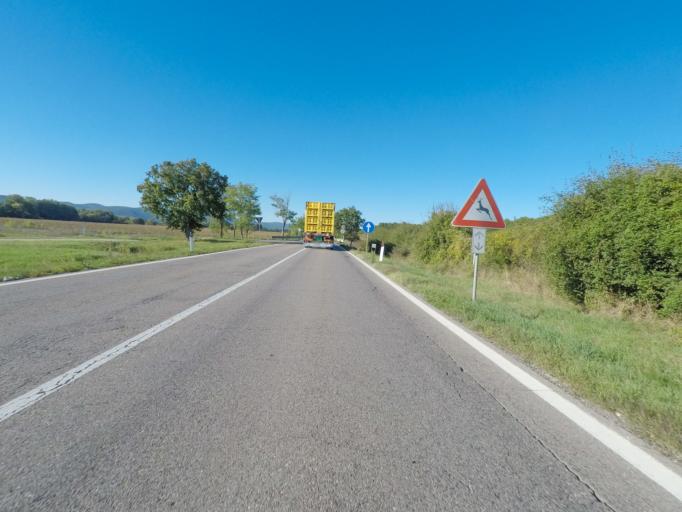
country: IT
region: Tuscany
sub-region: Provincia di Siena
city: Rosia
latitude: 43.2103
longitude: 11.2788
